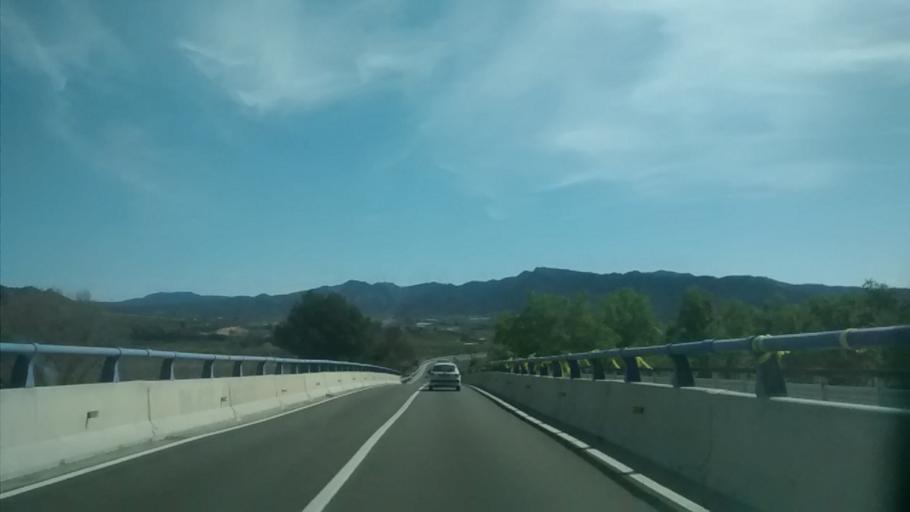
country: ES
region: Catalonia
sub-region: Provincia de Tarragona
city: Asco
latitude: 41.1874
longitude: 0.5704
